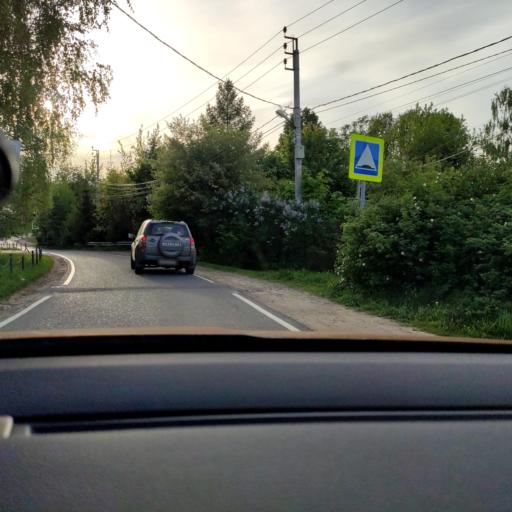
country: RU
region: Moskovskaya
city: Selyatino
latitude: 55.5266
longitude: 37.0111
